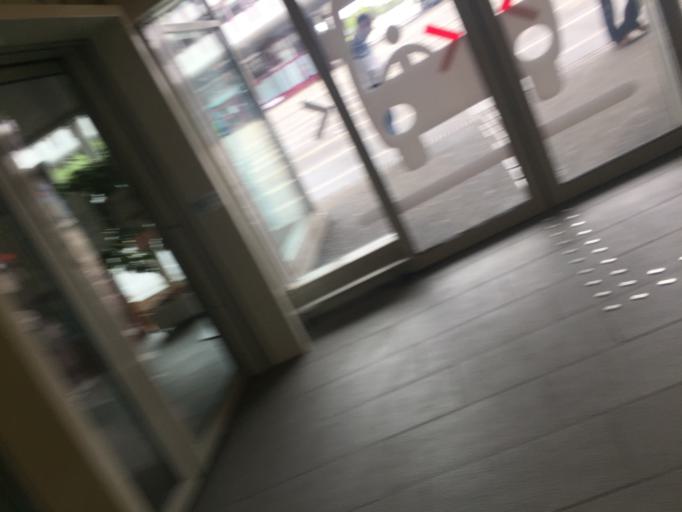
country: FR
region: Ile-de-France
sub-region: Departement des Yvelines
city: Montigny-le-Bretonneux
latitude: 48.7871
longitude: 2.0448
